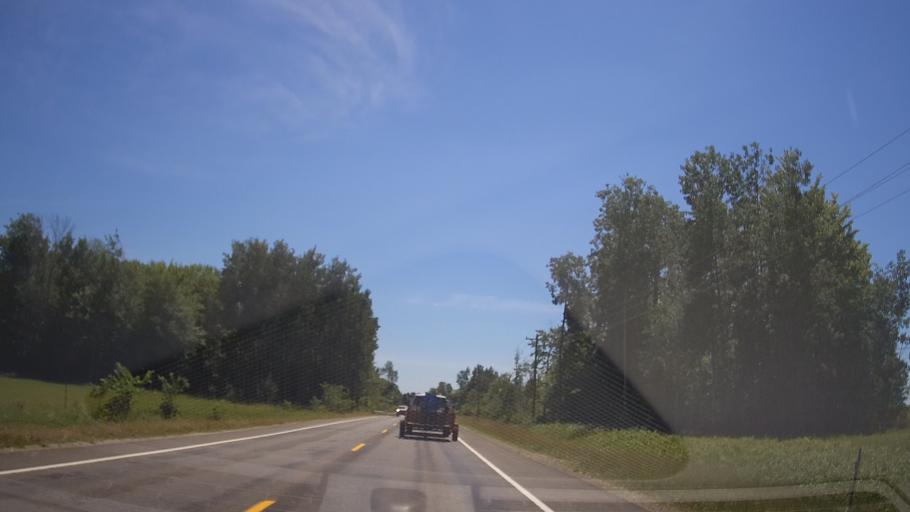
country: US
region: Michigan
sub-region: Grand Traverse County
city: Kingsley
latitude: 44.5947
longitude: -85.6963
